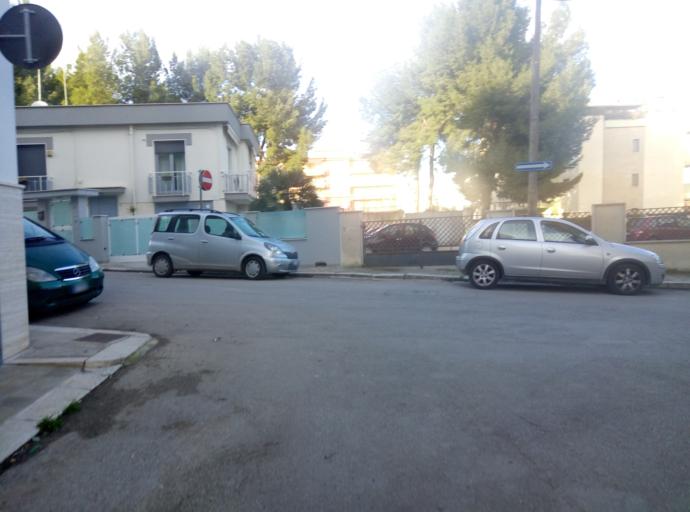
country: IT
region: Apulia
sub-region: Provincia di Bari
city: Ruvo di Puglia
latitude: 41.1182
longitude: 16.4896
